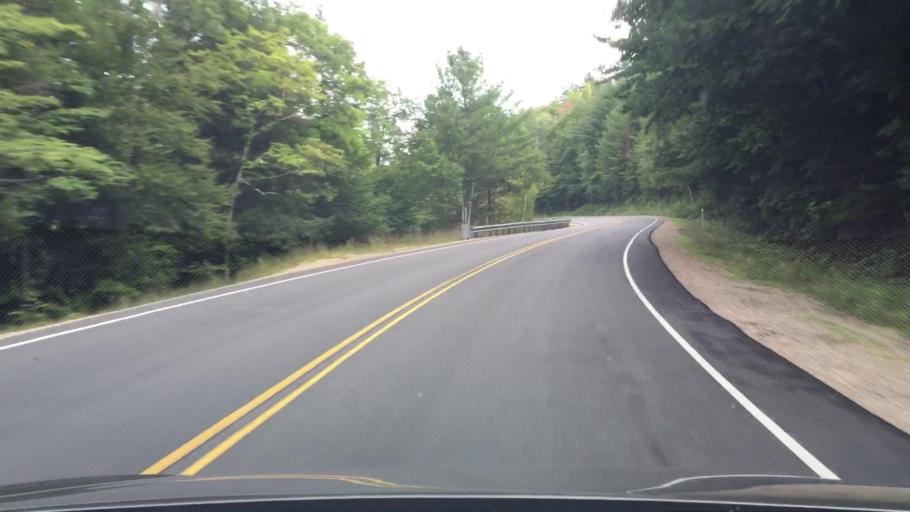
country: US
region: New Hampshire
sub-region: Carroll County
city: Conway
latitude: 44.0001
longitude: -71.2303
